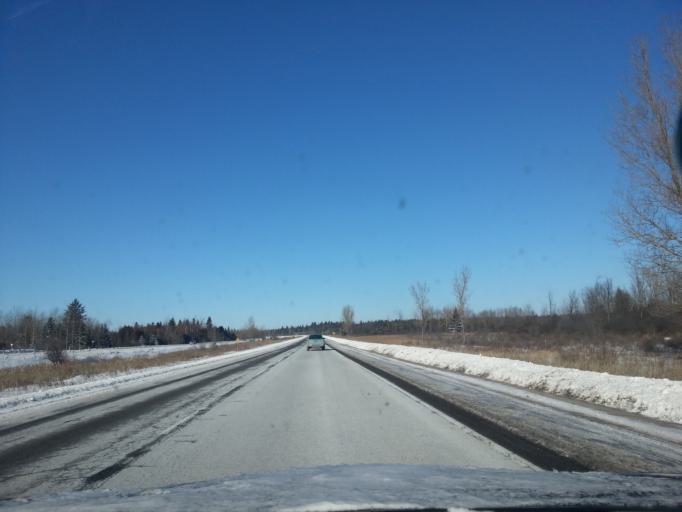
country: CA
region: Ontario
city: Bells Corners
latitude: 45.2870
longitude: -76.0072
